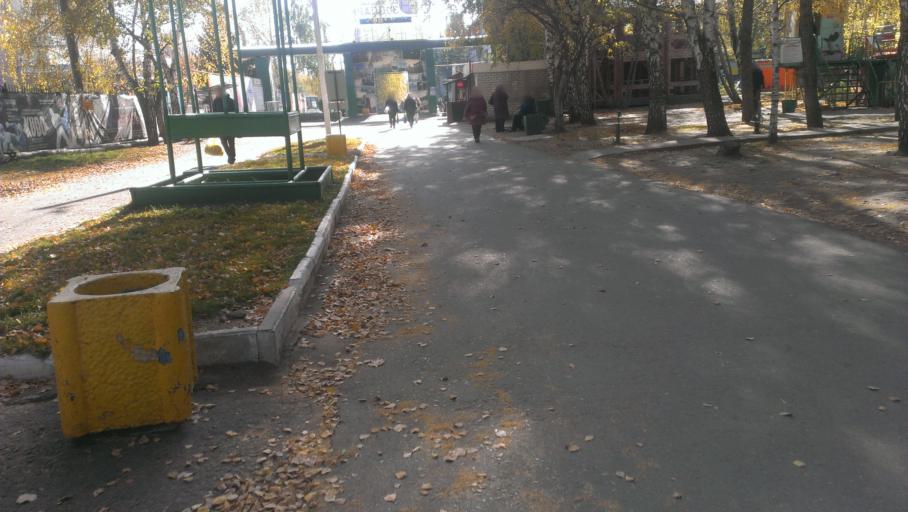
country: RU
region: Altai Krai
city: Novosilikatnyy
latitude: 53.3557
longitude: 83.6844
